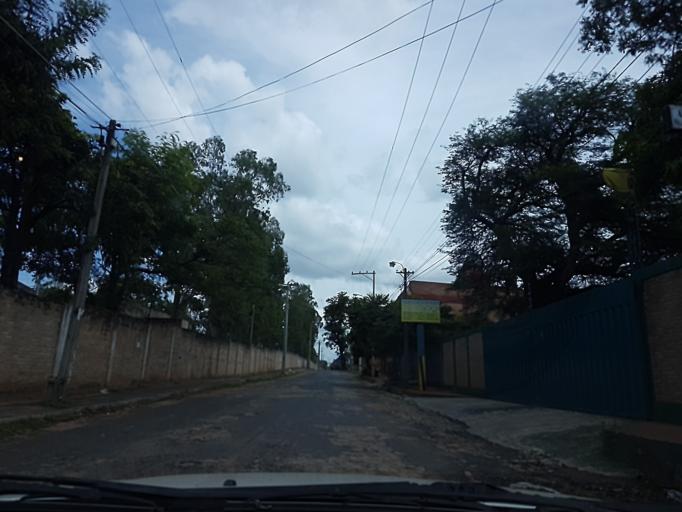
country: PY
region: Central
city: Colonia Mariano Roque Alonso
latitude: -25.2298
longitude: -57.5304
